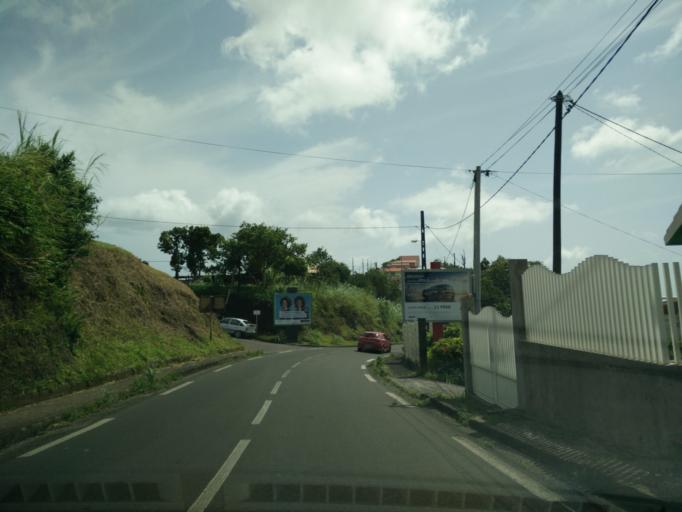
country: MQ
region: Martinique
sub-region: Martinique
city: Le Morne-Rouge
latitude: 14.7710
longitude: -61.1382
